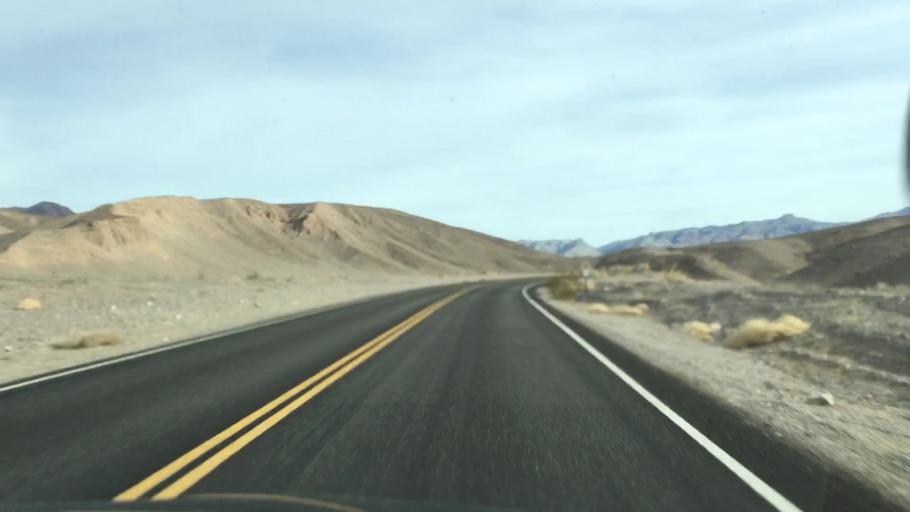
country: US
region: Nevada
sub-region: Nye County
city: Beatty
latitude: 36.6543
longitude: -117.0265
